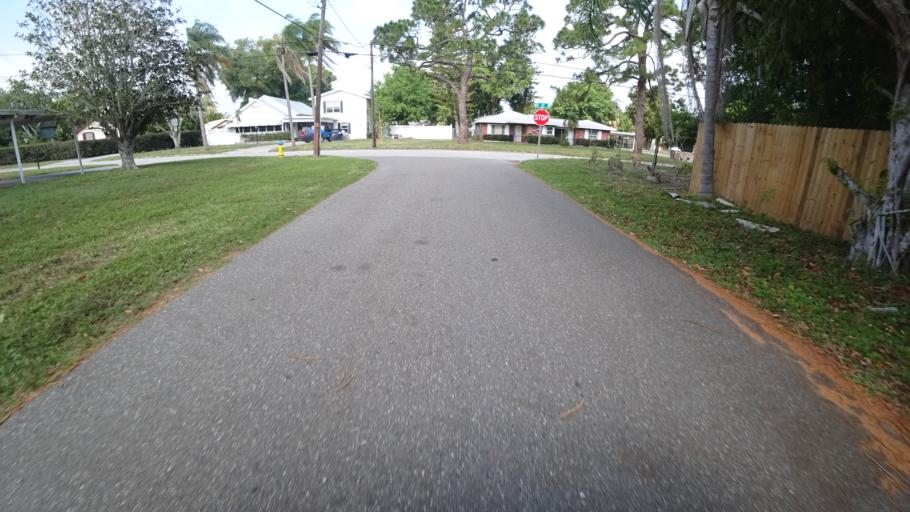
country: US
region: Florida
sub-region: Manatee County
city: West Bradenton
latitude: 27.4982
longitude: -82.6036
